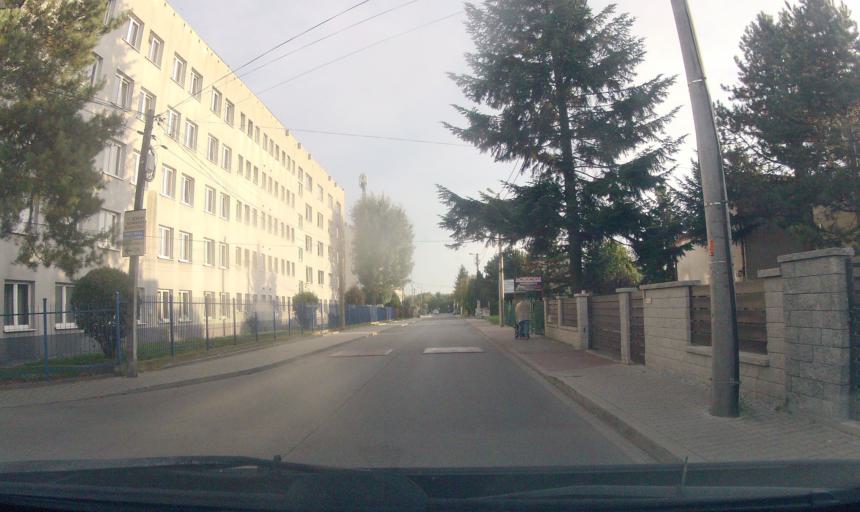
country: PL
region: Lesser Poland Voivodeship
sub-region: Krakow
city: Krakow
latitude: 50.0362
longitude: 19.9970
